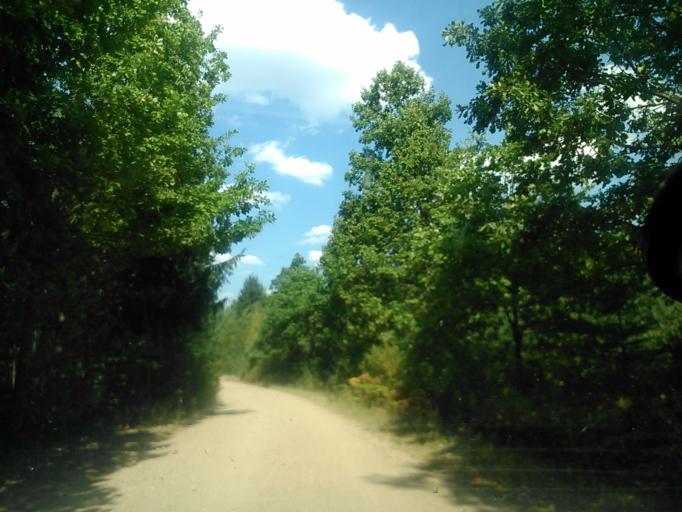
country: PL
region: Masovian Voivodeship
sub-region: Powiat ostrolecki
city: Czarnia
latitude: 53.3397
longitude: 21.1947
